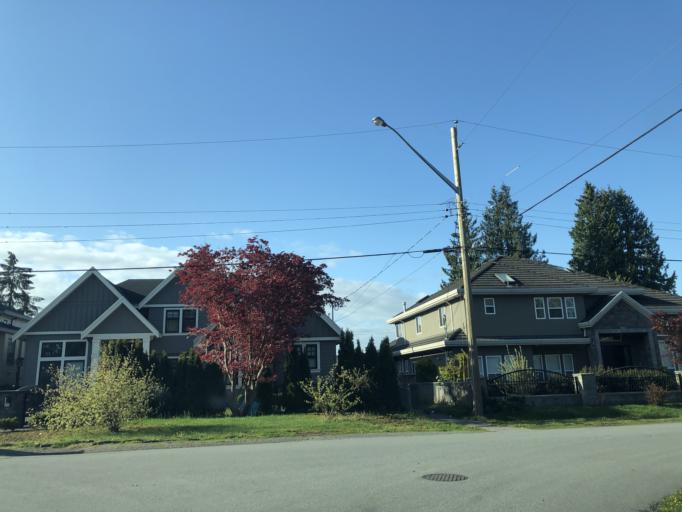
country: CA
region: British Columbia
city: Richmond
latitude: 49.1417
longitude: -123.1170
